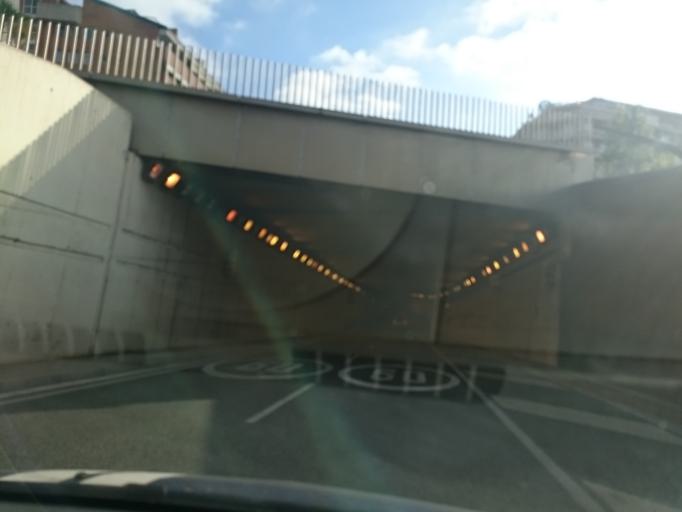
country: ES
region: Catalonia
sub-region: Provincia de Barcelona
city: les Corts
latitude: 41.3853
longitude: 2.1272
